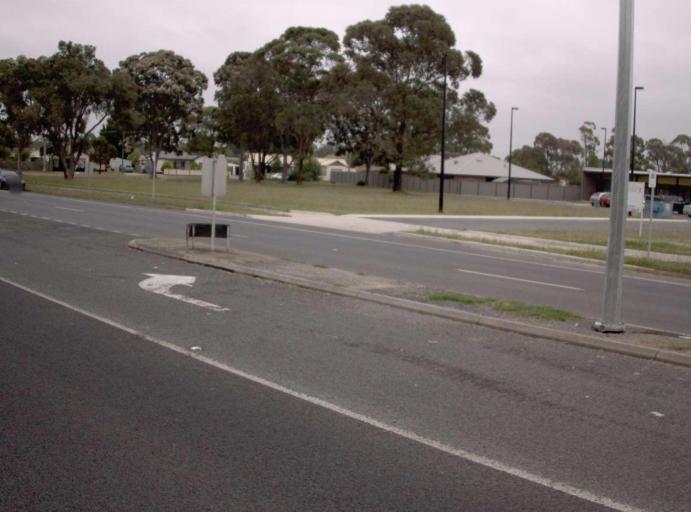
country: AU
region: Victoria
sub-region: Latrobe
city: Traralgon
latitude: -38.2027
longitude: 146.5213
